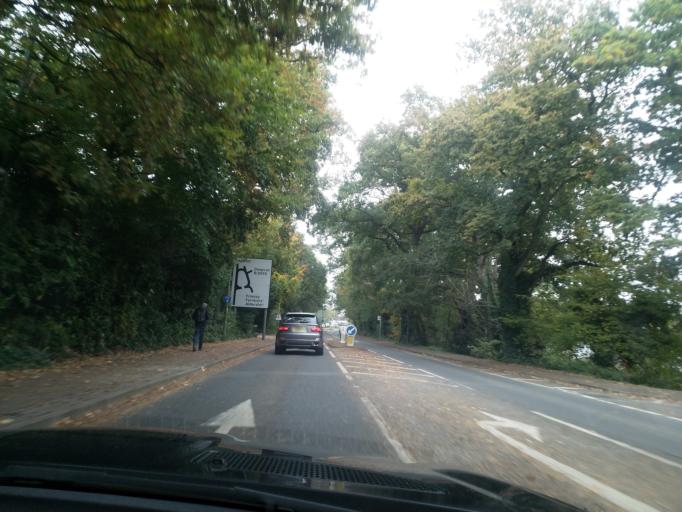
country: GB
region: England
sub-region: Surrey
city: Camberley
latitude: 51.3474
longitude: -0.7178
